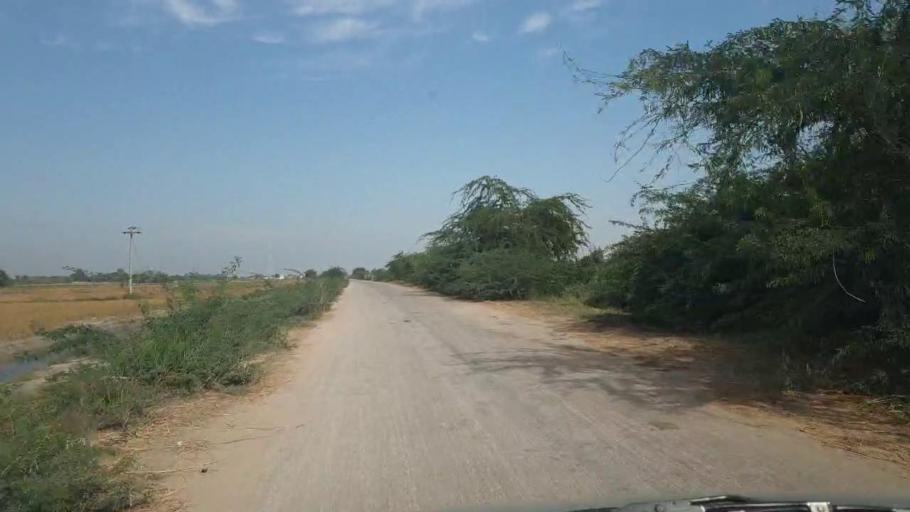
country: PK
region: Sindh
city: Tando Bago
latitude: 24.8840
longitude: 69.0015
